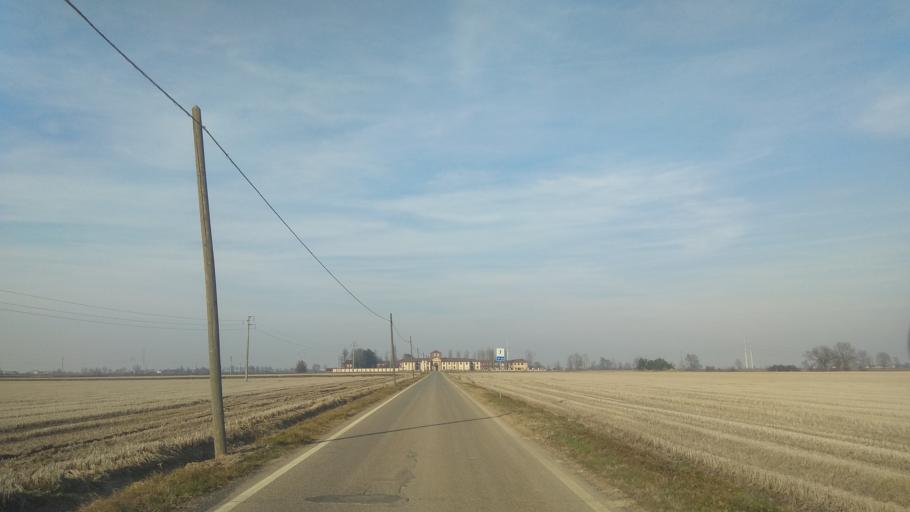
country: IT
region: Piedmont
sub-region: Provincia di Vercelli
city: Ronsecco
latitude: 45.2444
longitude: 8.2350
